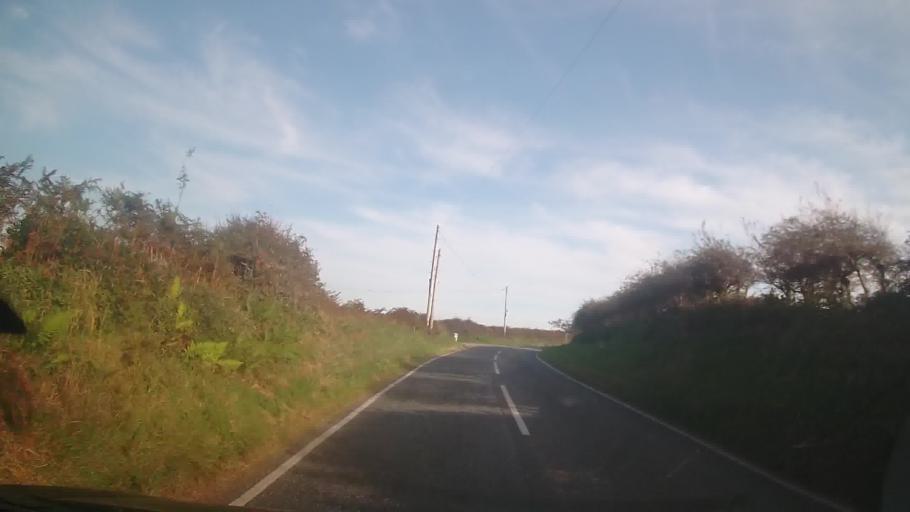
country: GB
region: Wales
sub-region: Pembrokeshire
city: Fishguard
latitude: 51.9703
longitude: -4.9064
